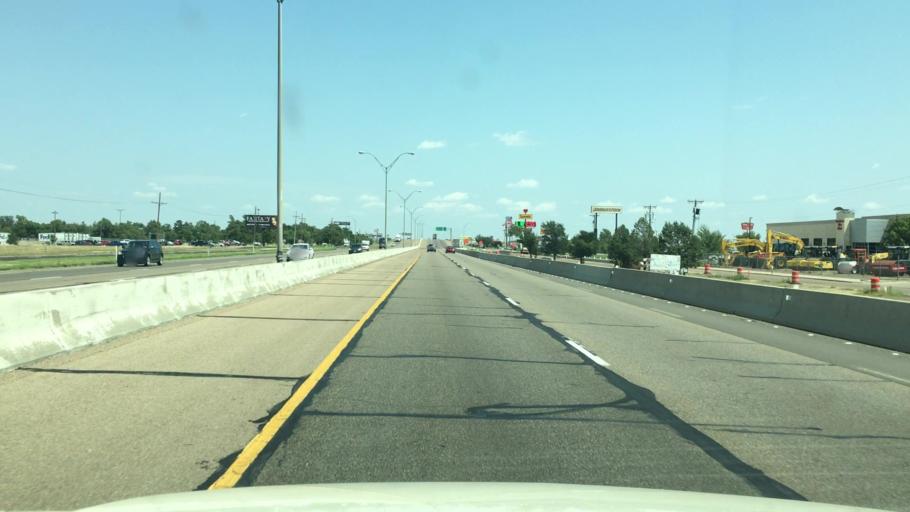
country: US
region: Texas
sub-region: Potter County
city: Amarillo
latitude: 35.1926
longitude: -101.7675
